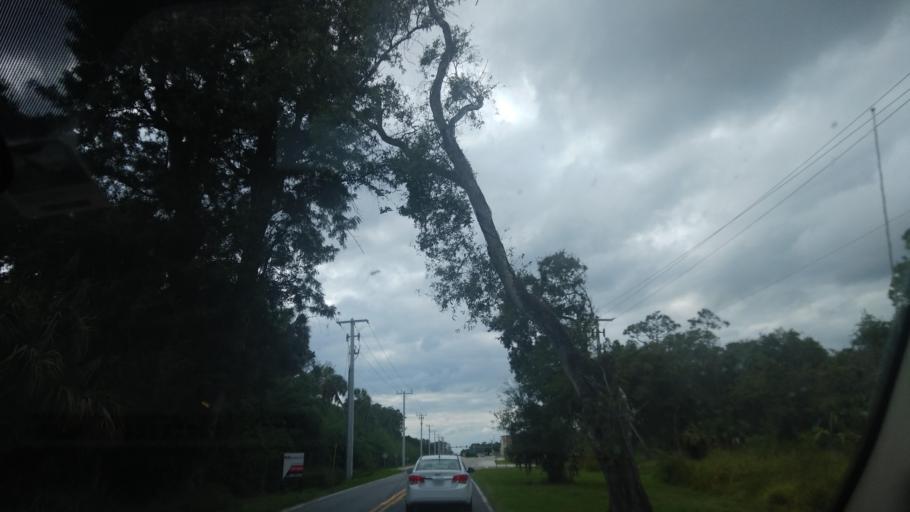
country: US
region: Florida
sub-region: Saint Lucie County
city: Lakewood Park
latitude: 27.5210
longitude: -80.3934
